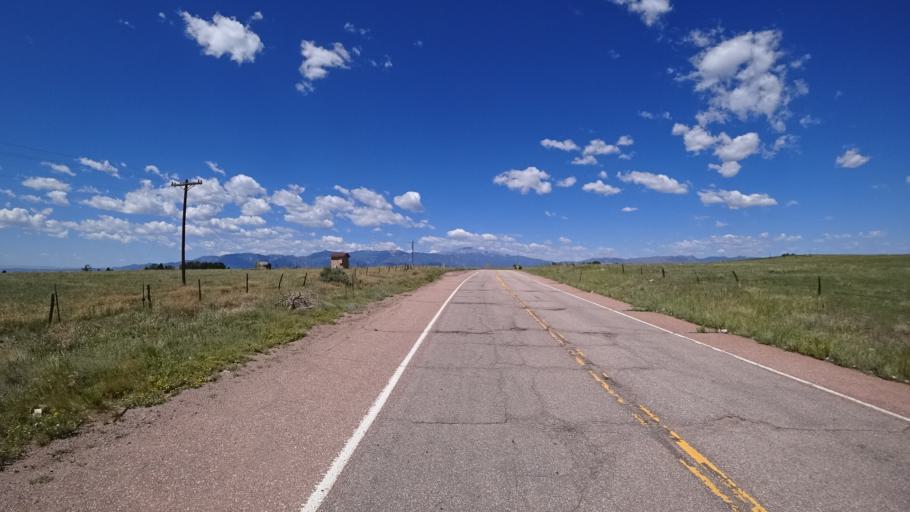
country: US
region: Colorado
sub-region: El Paso County
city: Cimarron Hills
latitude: 38.8374
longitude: -104.6781
